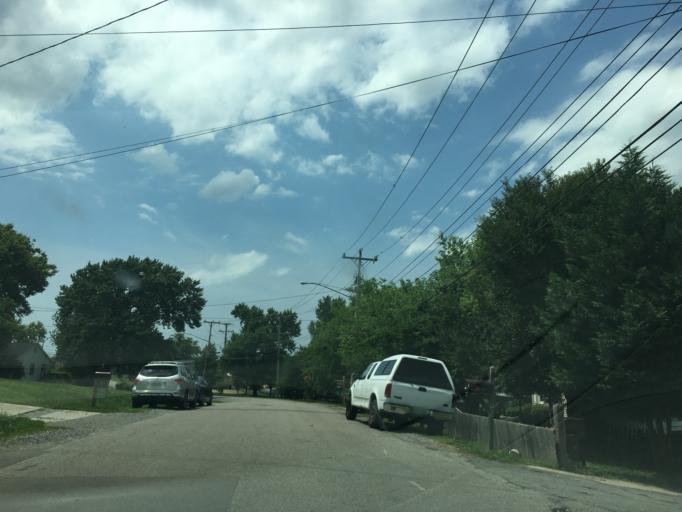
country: US
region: Tennessee
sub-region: Davidson County
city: Nashville
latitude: 36.1318
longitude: -86.7509
